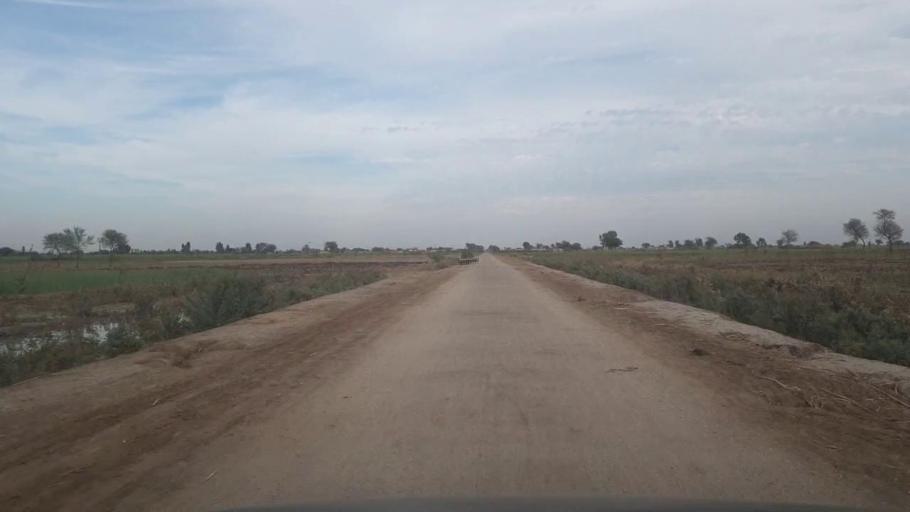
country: PK
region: Sindh
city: Samaro
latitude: 25.3226
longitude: 69.2524
